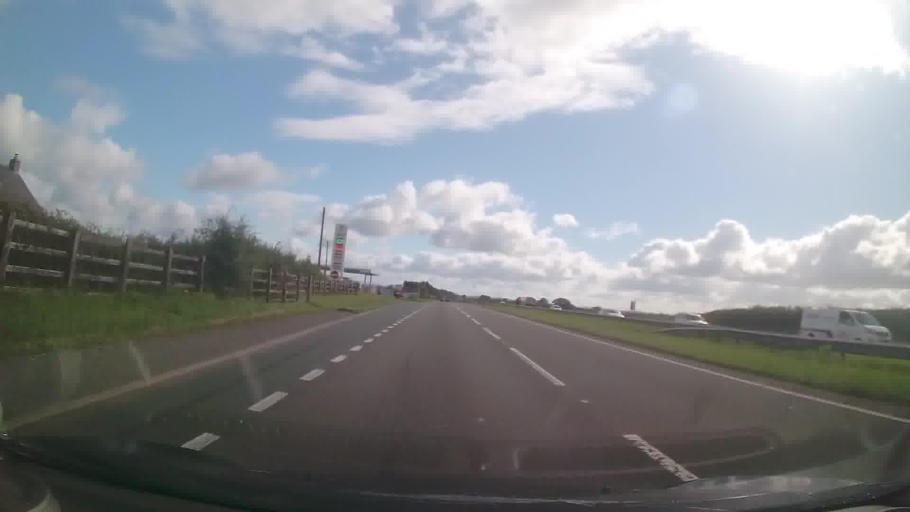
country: GB
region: Wales
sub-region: Carmarthenshire
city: Llanddarog
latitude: 51.8396
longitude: -4.2199
